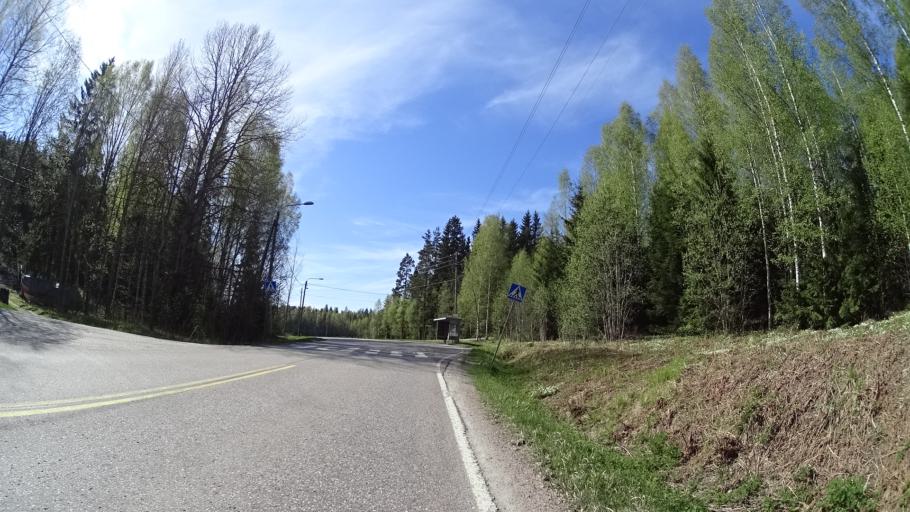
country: FI
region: Uusimaa
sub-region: Helsinki
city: Nurmijaervi
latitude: 60.3828
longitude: 24.8363
